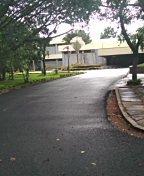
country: IN
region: Karnataka
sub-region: Mysore
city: Mysore
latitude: 12.3056
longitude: 76.6748
